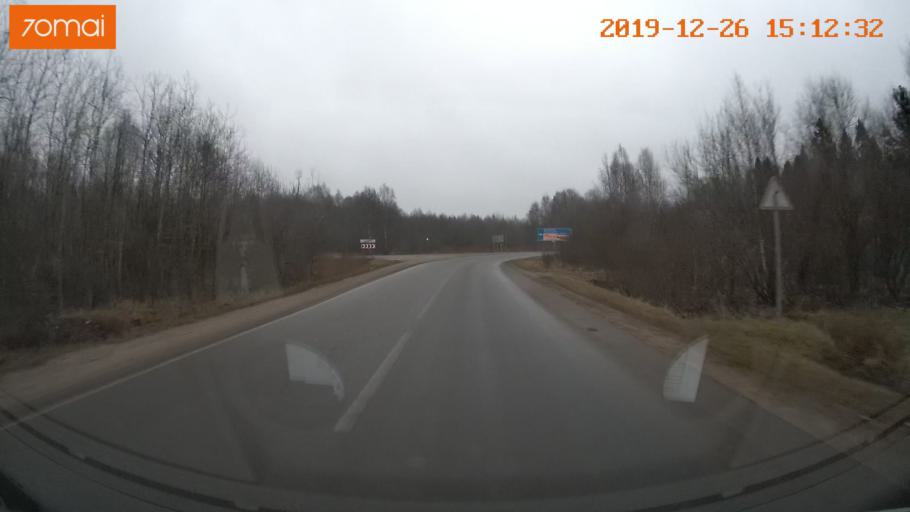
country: RU
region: Jaroslavl
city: Rybinsk
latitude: 58.1269
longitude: 38.8776
